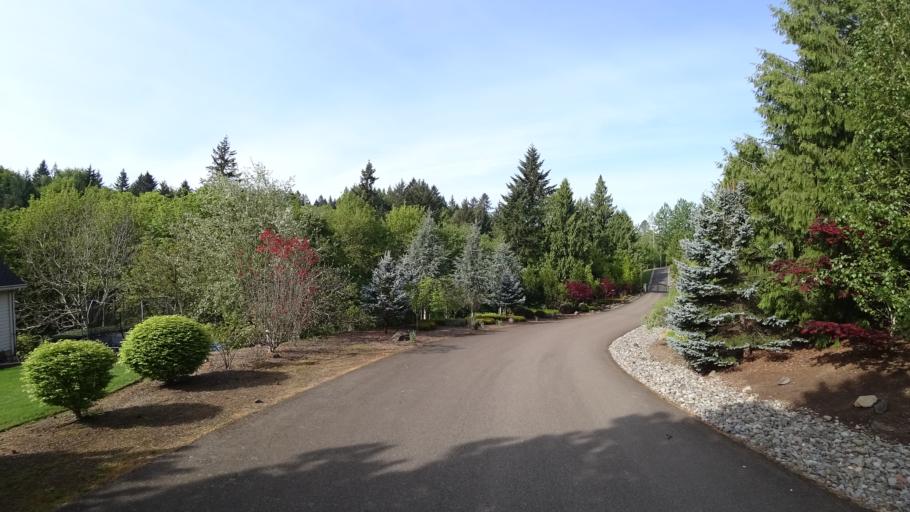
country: US
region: Oregon
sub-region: Washington County
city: Aloha
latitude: 45.4439
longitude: -122.8507
